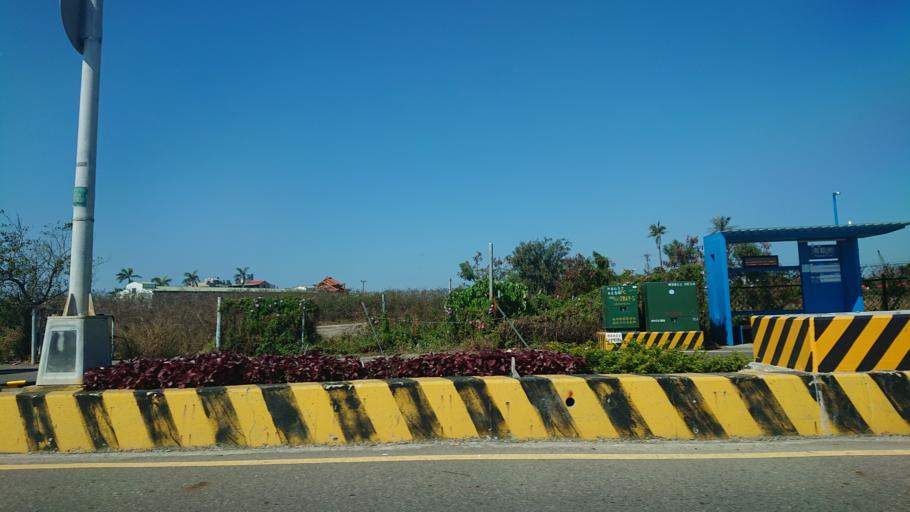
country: TW
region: Taiwan
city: Xinying
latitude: 23.2858
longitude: 120.1396
